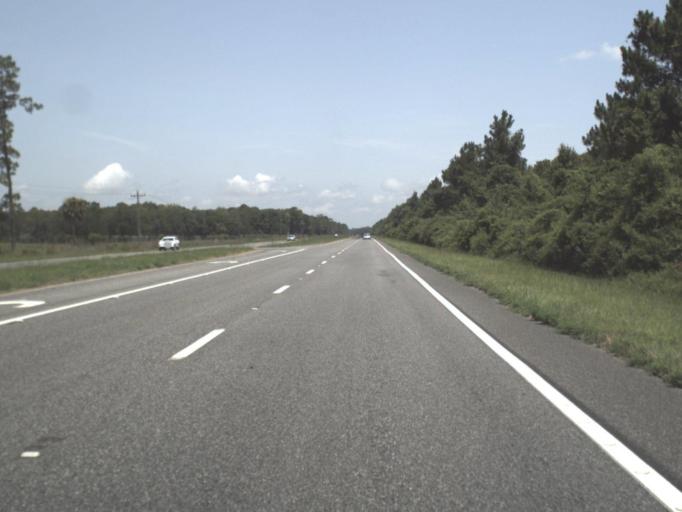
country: US
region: Florida
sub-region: Taylor County
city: Steinhatchee
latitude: 29.8543
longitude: -83.3831
